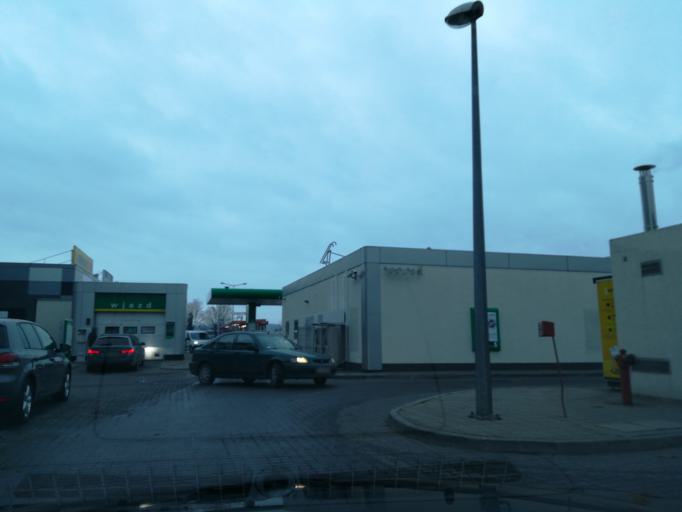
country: PL
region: Subcarpathian Voivodeship
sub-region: Rzeszow
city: Rzeszow
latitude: 50.0186
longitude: 22.0144
